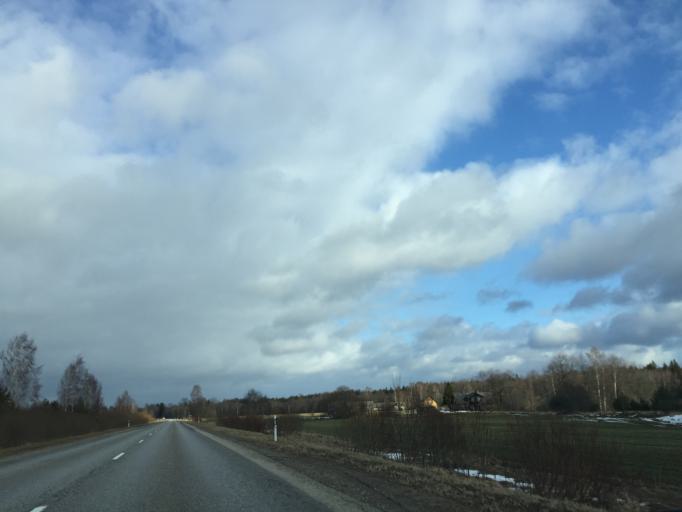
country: LV
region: Aloja
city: Staicele
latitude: 57.8802
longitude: 24.5944
